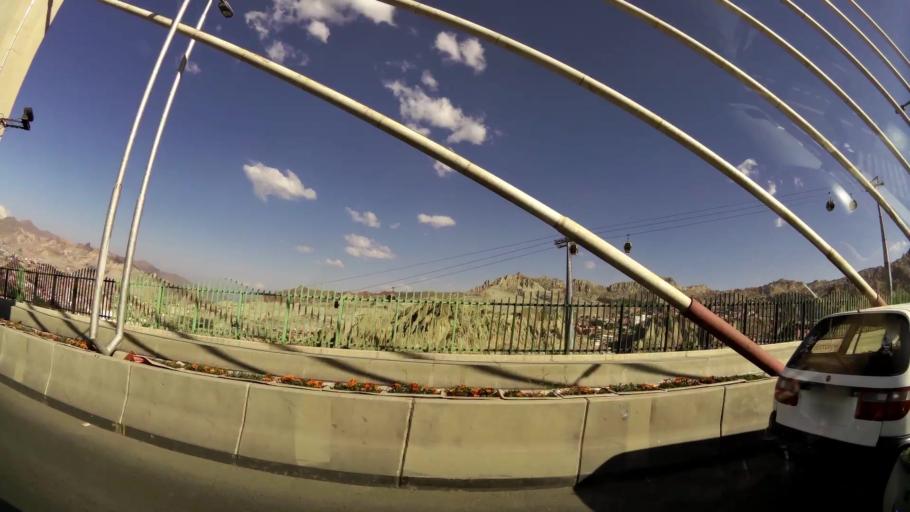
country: BO
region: La Paz
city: La Paz
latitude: -16.5167
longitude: -68.1208
